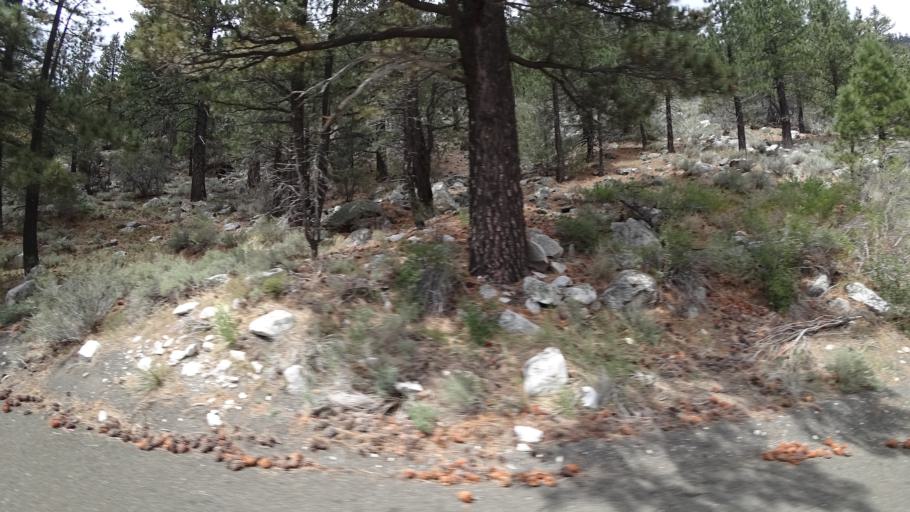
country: US
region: California
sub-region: Mono County
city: Bridgeport
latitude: 38.4013
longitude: -119.4535
